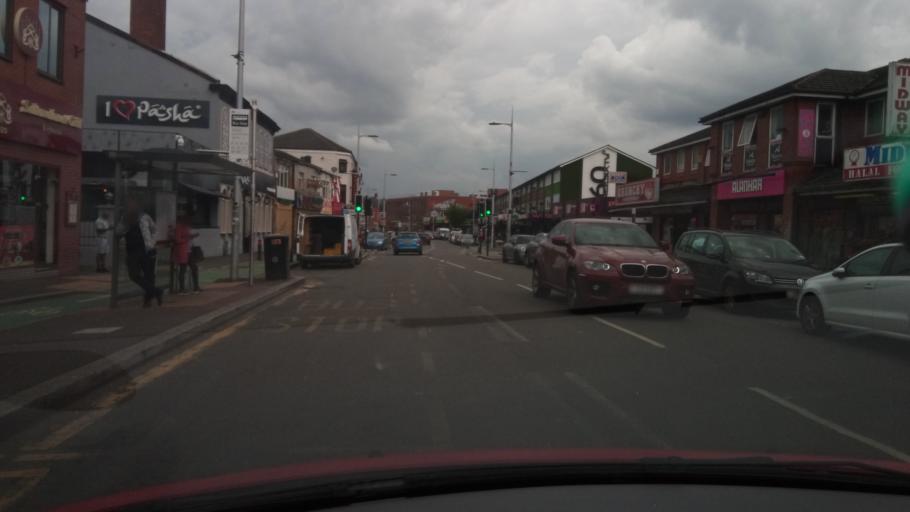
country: GB
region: England
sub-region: Manchester
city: Fallowfield
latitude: 53.4557
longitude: -2.2253
